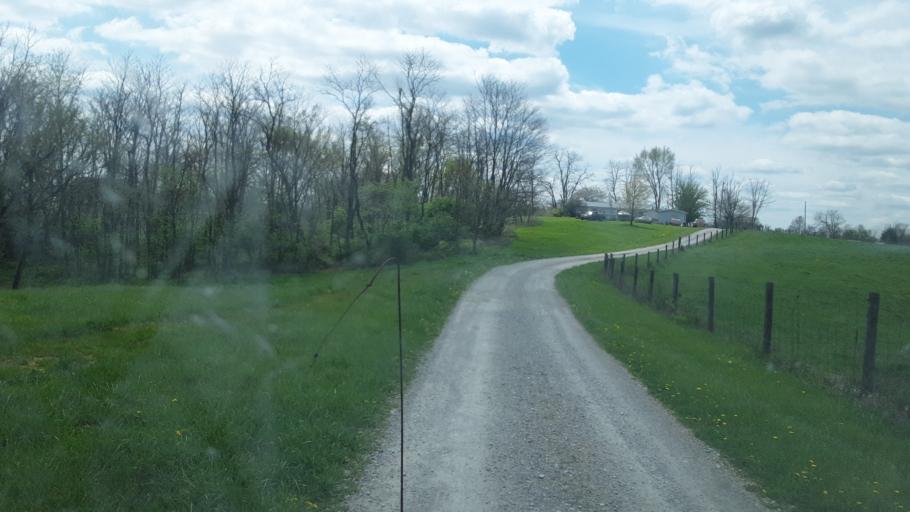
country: US
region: Kentucky
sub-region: Gallatin County
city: Warsaw
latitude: 38.6766
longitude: -84.8124
